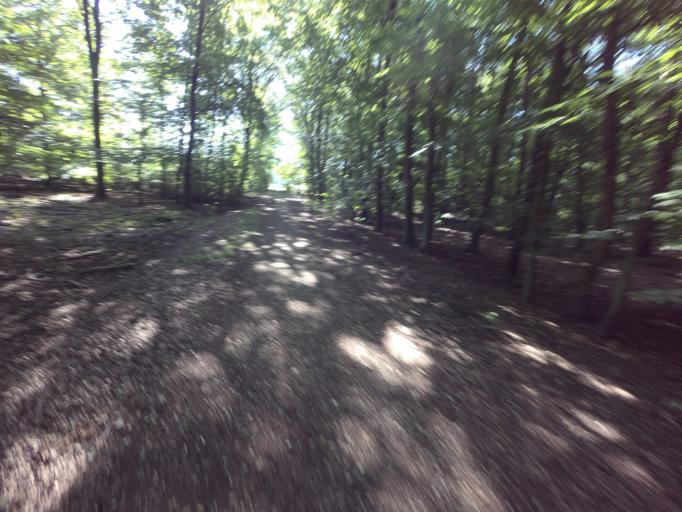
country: DE
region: North Rhine-Westphalia
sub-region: Regierungsbezirk Koln
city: Wassenberg
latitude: 51.1551
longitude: 6.1601
